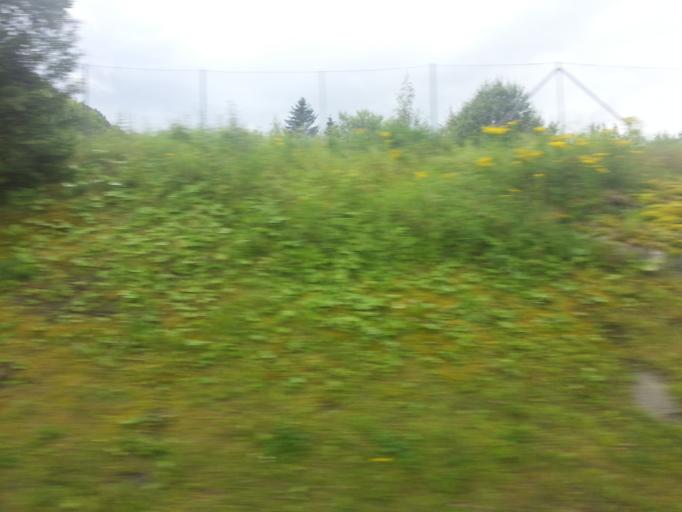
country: NO
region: Sor-Trondelag
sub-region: Malvik
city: Hommelvik
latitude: 63.4120
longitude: 10.7714
